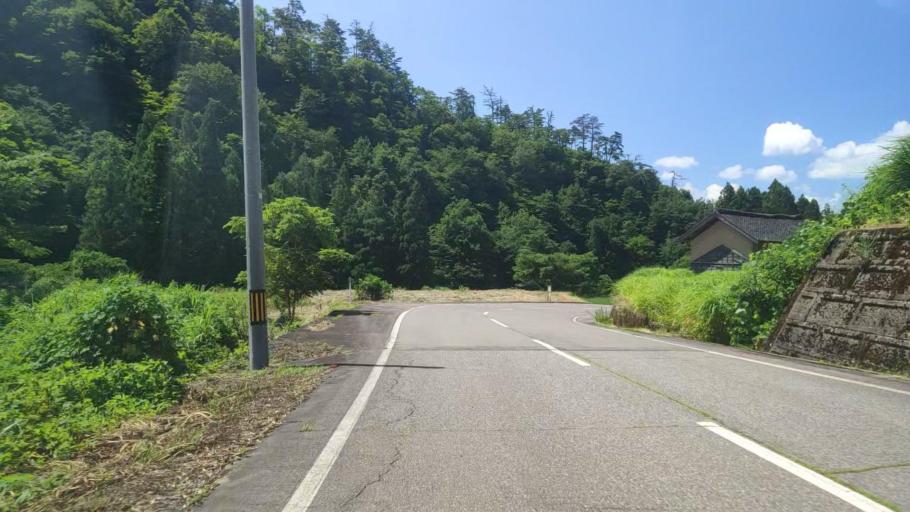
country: JP
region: Fukui
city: Katsuyama
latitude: 36.1124
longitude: 136.5028
